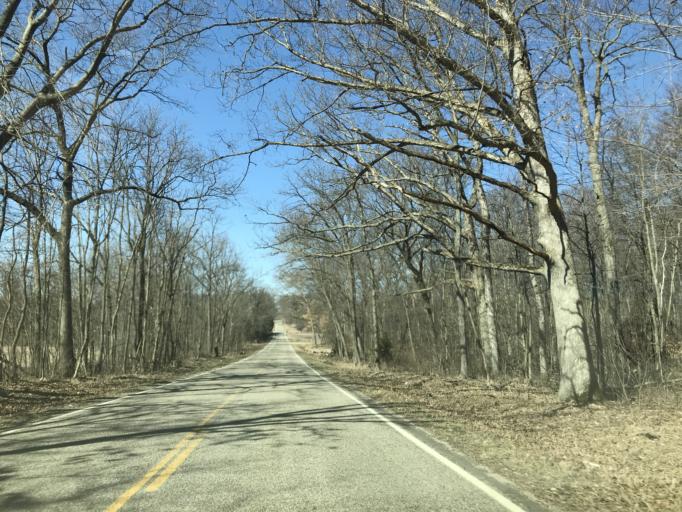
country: US
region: Michigan
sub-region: Hillsdale County
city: Litchfield
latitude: 41.9856
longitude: -84.7462
